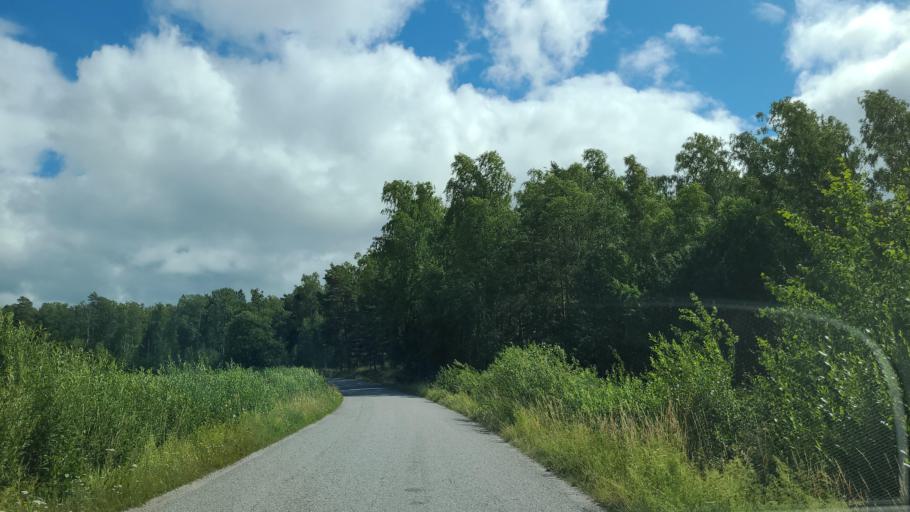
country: FI
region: Varsinais-Suomi
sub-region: Aboland-Turunmaa
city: Nagu
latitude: 60.1755
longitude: 22.0261
